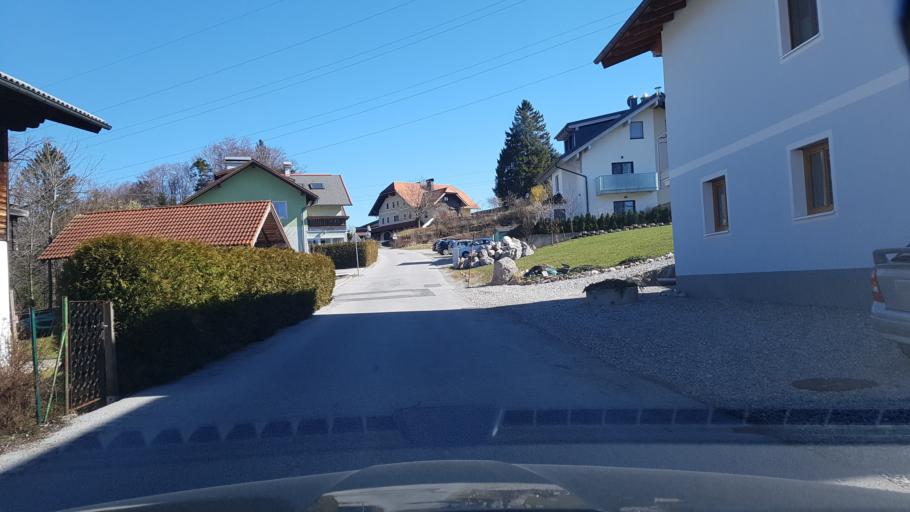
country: AT
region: Salzburg
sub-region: Politischer Bezirk Salzburg-Umgebung
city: Koppl
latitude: 47.8062
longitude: 13.1568
